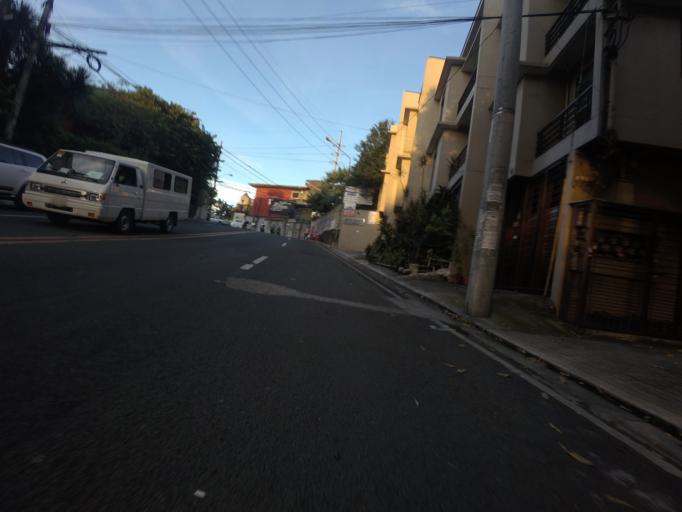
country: PH
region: Metro Manila
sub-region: San Juan
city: San Juan
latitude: 14.5973
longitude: 121.0300
